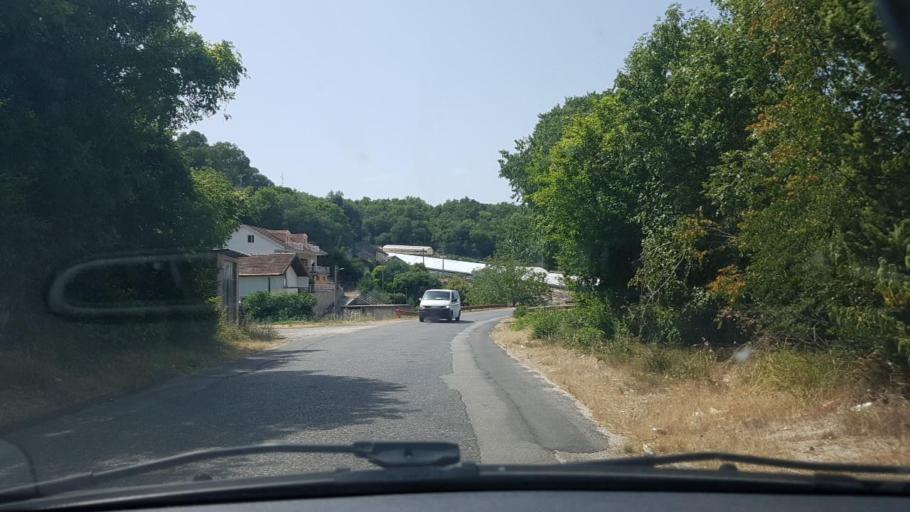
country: BA
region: Federation of Bosnia and Herzegovina
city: Tasovcici
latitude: 43.0173
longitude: 17.7748
